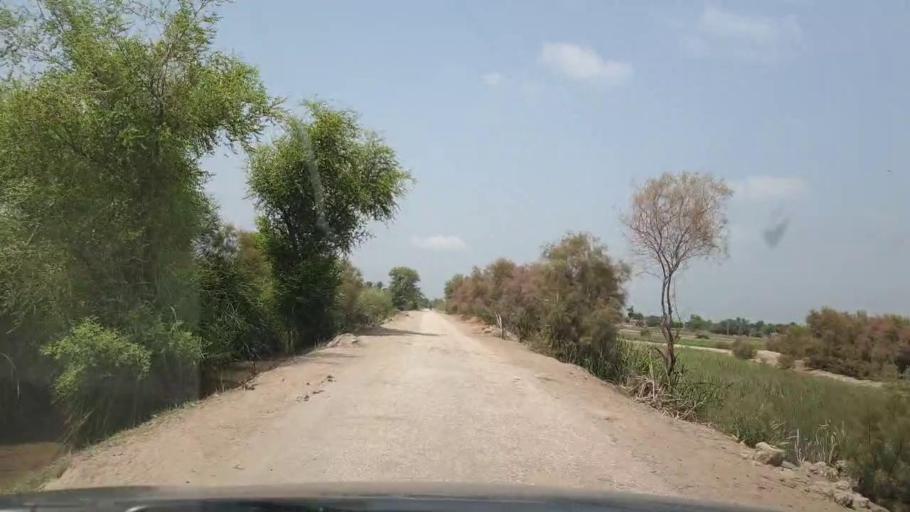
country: PK
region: Sindh
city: Ratodero
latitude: 27.8967
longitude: 68.3214
